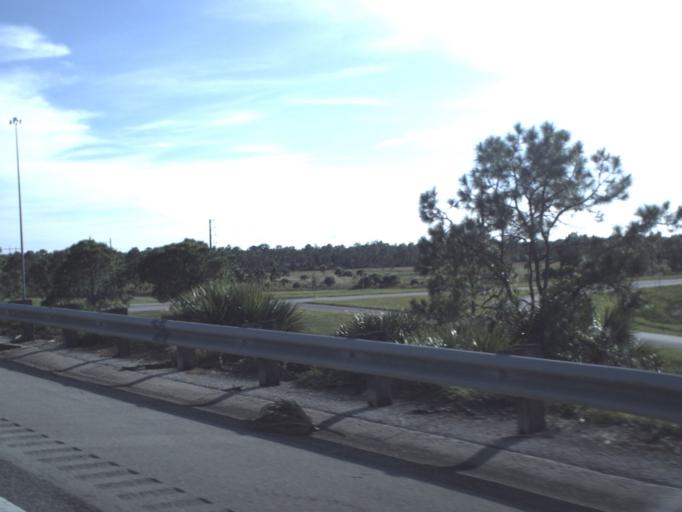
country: US
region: Florida
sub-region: Charlotte County
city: Charlotte Park
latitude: 26.8595
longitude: -81.9716
